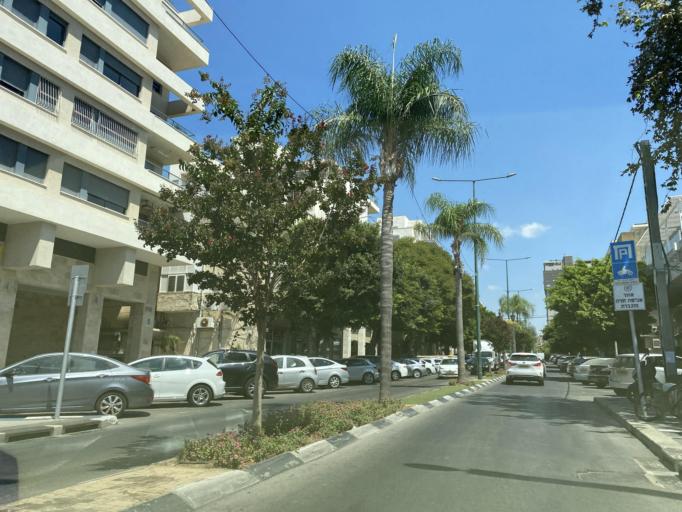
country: IL
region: Tel Aviv
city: Herzliyya
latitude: 32.1671
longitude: 34.8462
